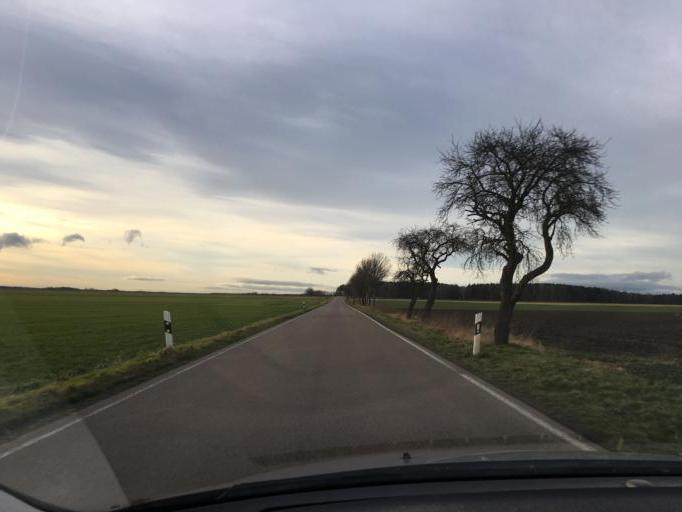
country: DE
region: Saxony
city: Belgershain
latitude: 51.2206
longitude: 12.5167
